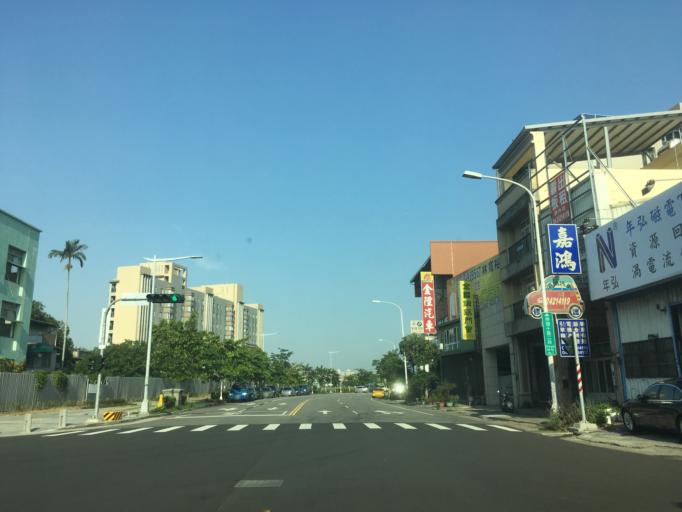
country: TW
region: Taiwan
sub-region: Taichung City
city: Taichung
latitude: 24.1883
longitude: 120.6825
